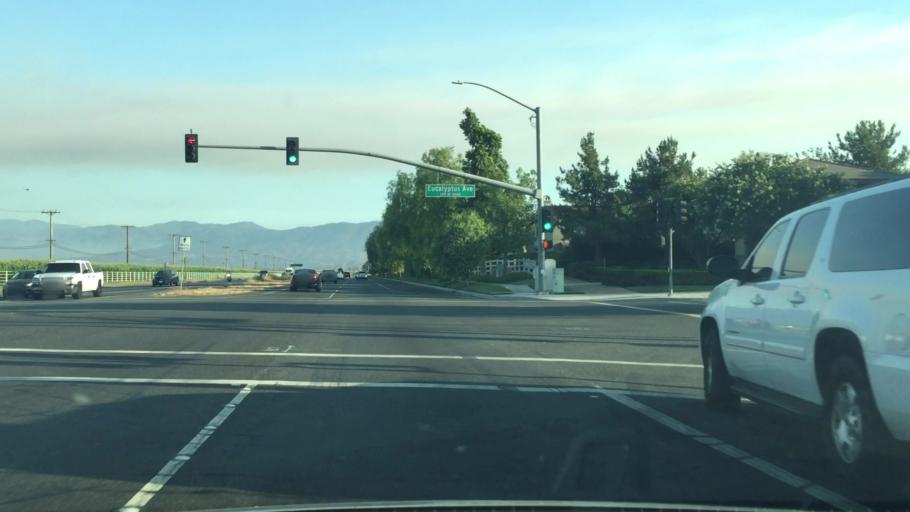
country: US
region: California
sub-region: San Bernardino County
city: Chino
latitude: 33.9904
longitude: -117.6509
